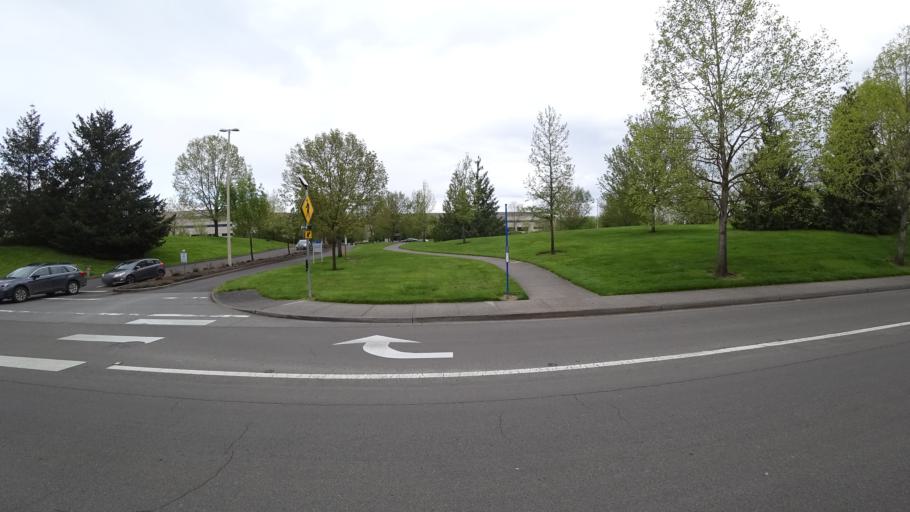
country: US
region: Oregon
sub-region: Washington County
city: Hillsboro
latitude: 45.5422
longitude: -122.9664
